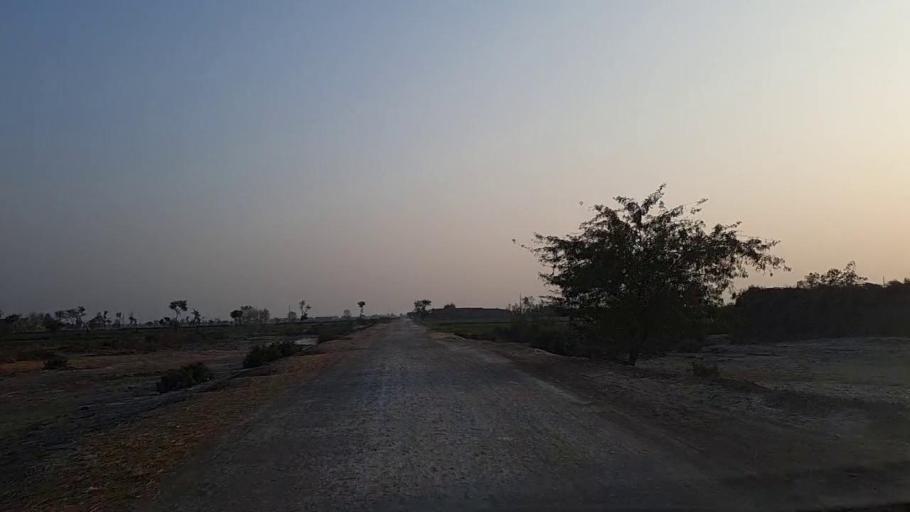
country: PK
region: Sindh
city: Daur
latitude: 26.4312
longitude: 68.3680
